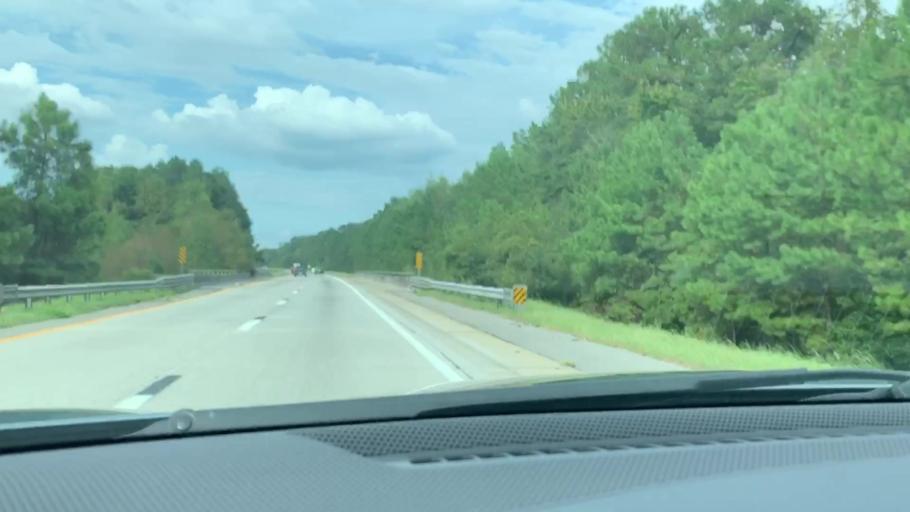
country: US
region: South Carolina
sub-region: Dorchester County
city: Saint George
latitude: 33.0977
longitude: -80.6454
